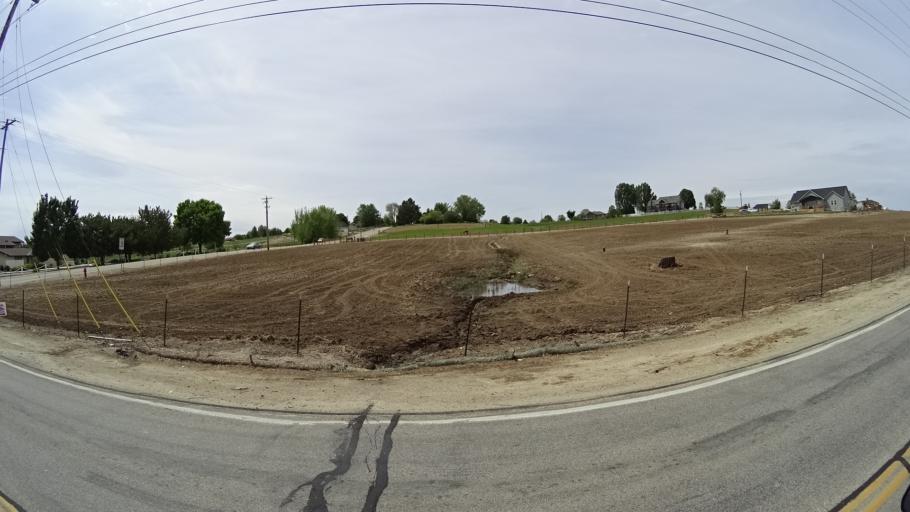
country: US
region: Idaho
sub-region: Ada County
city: Meridian
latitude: 43.5613
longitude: -116.3751
